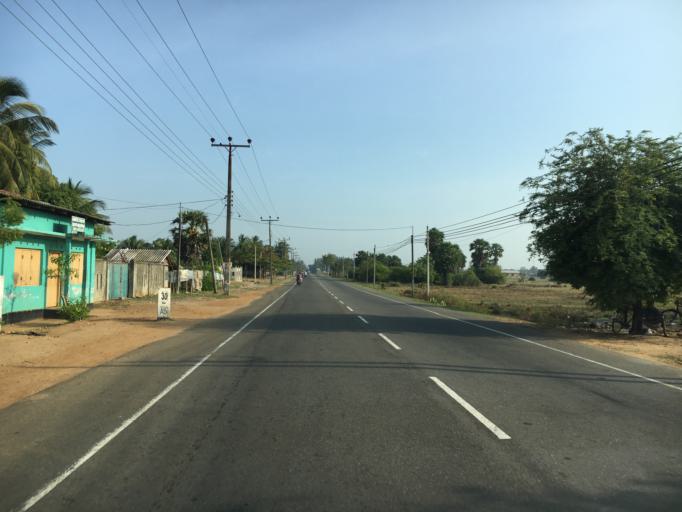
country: LK
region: Eastern Province
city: Eravur Town
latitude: 7.8950
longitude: 81.5368
